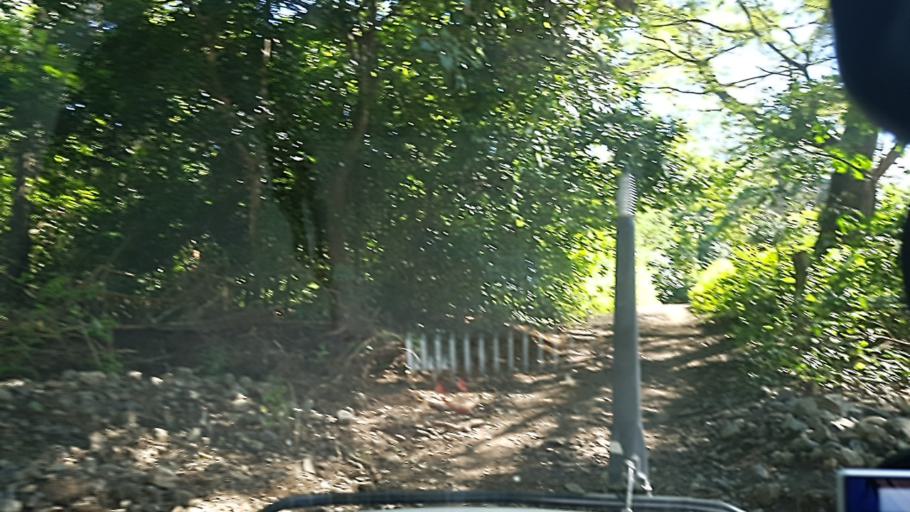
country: NI
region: Rivas
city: Tola
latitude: 11.5612
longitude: -86.0868
